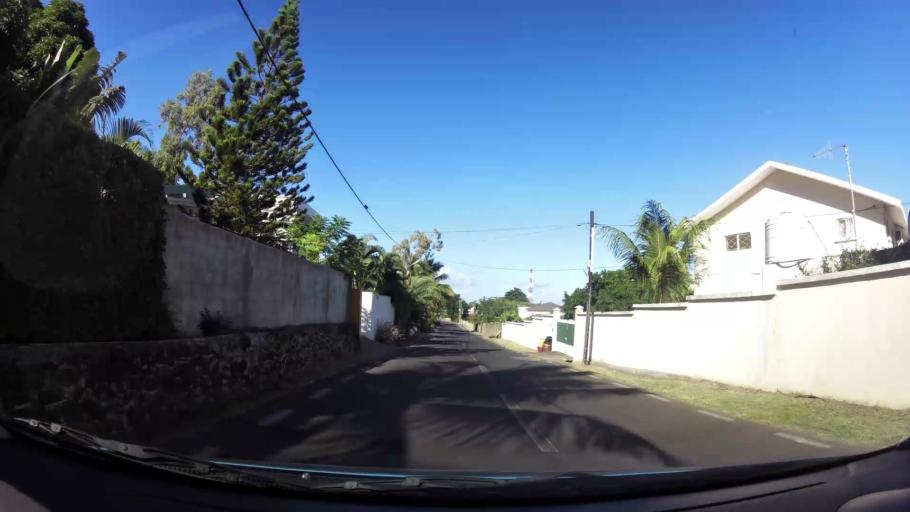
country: MU
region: Black River
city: Grande Riviere Noire
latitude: -20.3476
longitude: 57.3659
